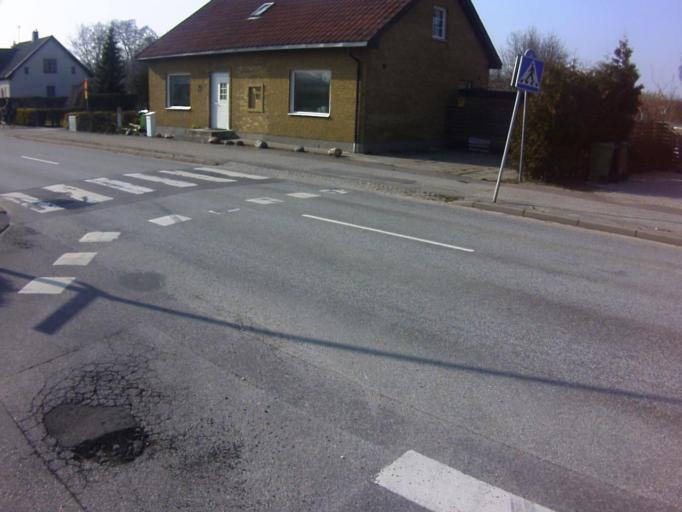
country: SE
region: Skane
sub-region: Kavlinge Kommun
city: Kaevlinge
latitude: 55.7939
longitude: 13.1336
